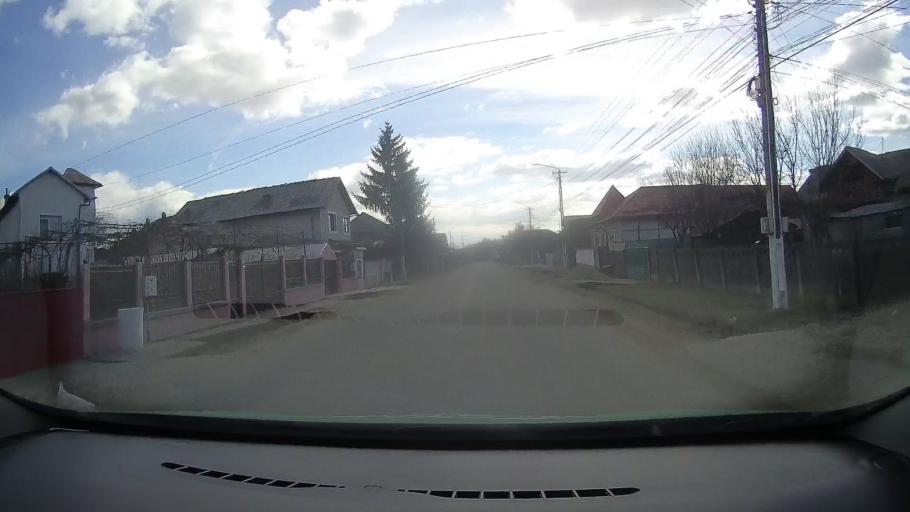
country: RO
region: Dambovita
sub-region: Comuna Doicesti
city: Doicesti
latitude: 44.9786
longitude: 25.3911
